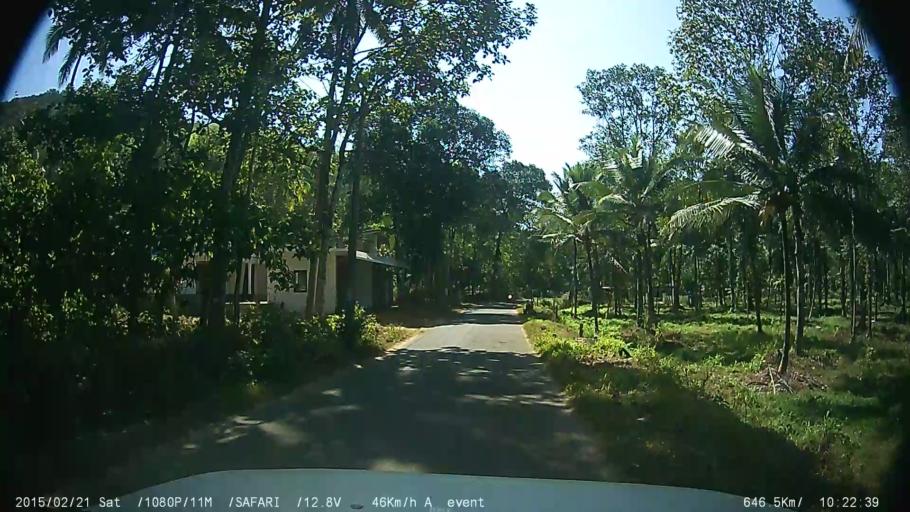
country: IN
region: Kerala
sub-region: Kottayam
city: Palackattumala
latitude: 9.8635
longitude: 76.6716
